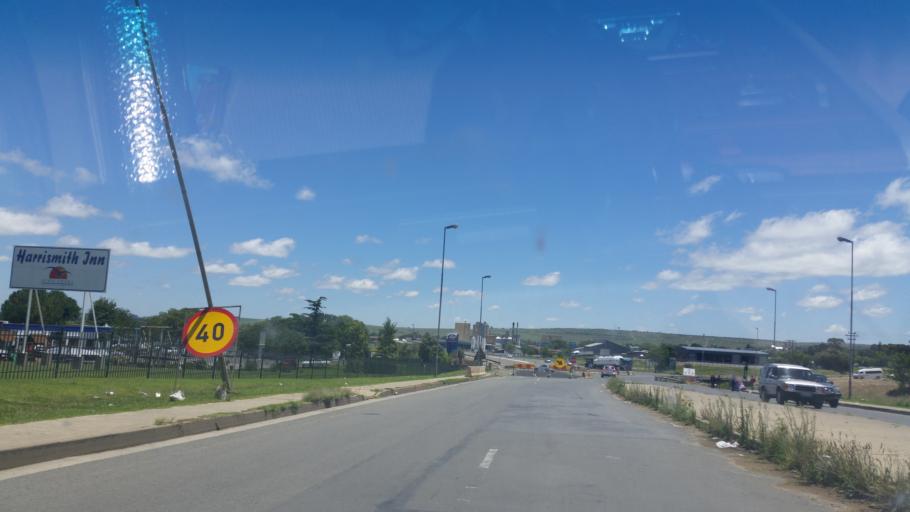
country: ZA
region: Orange Free State
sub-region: Thabo Mofutsanyana District Municipality
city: Harrismith
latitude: -28.2863
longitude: 29.1322
